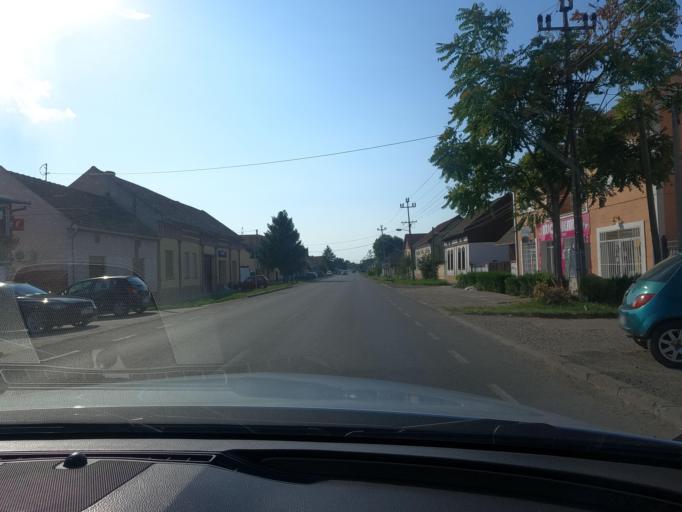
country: RS
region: Autonomna Pokrajina Vojvodina
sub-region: Juznobacki Okrug
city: Petrovaradin
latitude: 45.3005
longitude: 19.9377
